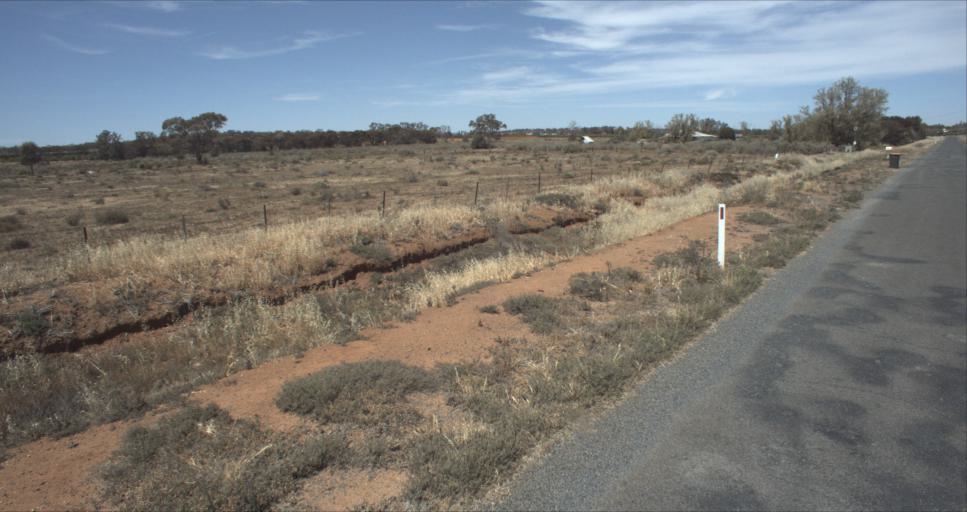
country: AU
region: New South Wales
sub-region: Leeton
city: Leeton
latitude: -34.6031
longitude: 146.4266
